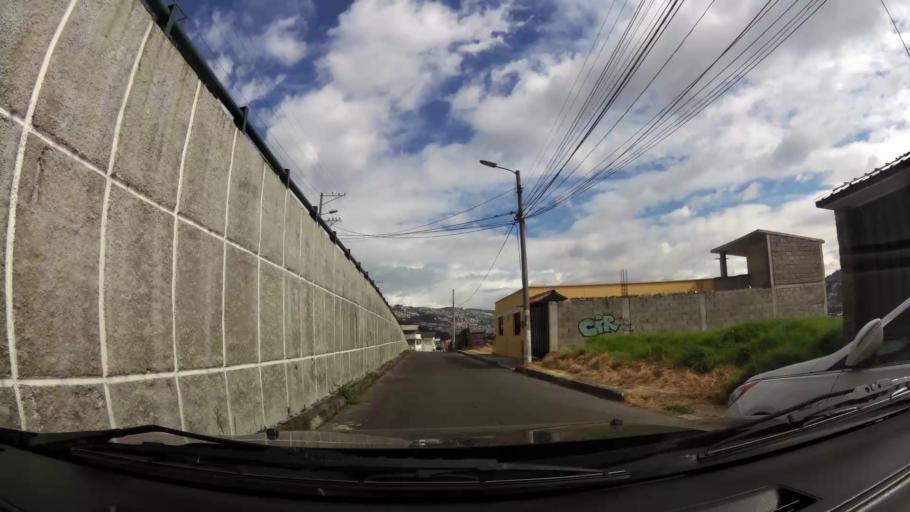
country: EC
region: Pichincha
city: Quito
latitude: -0.2206
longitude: -78.5037
